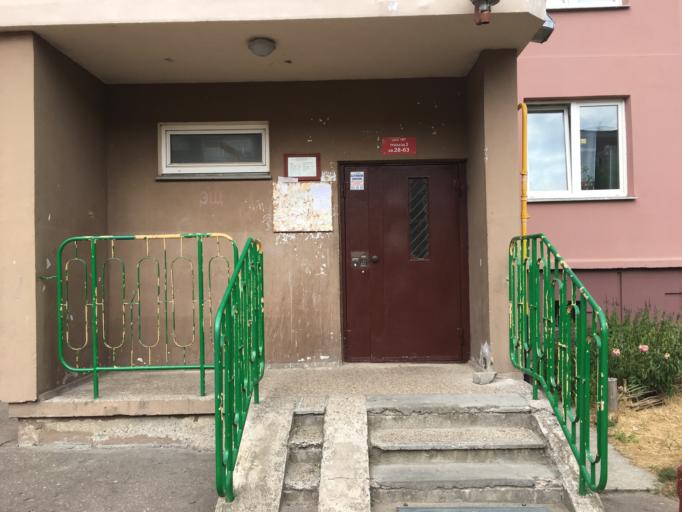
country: BY
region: Grodnenskaya
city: Hrodna
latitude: 53.7146
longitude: 23.8409
